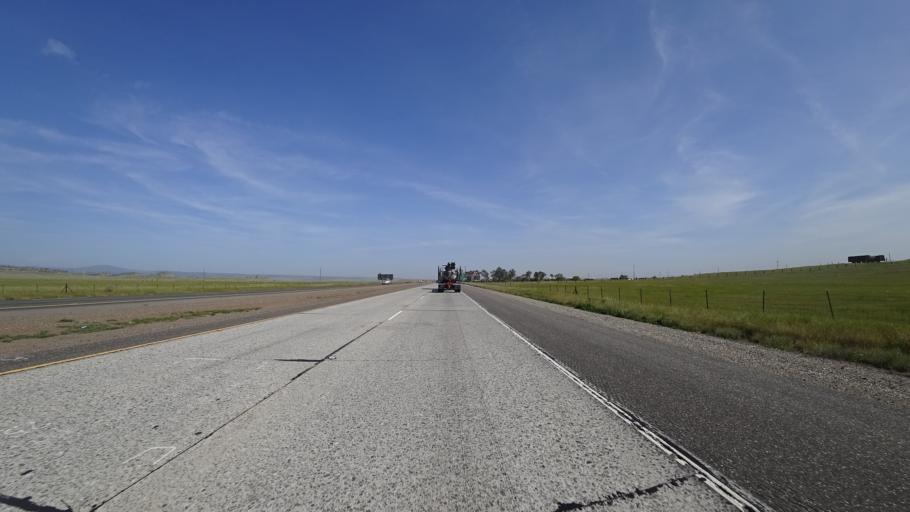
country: US
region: California
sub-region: Butte County
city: Durham
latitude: 39.6546
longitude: -121.7304
